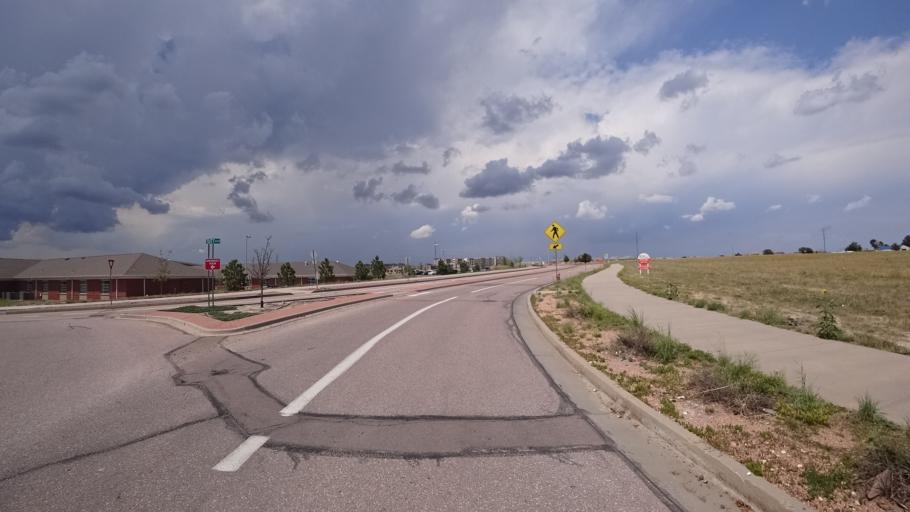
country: US
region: Colorado
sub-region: El Paso County
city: Black Forest
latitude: 38.9369
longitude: -104.7114
